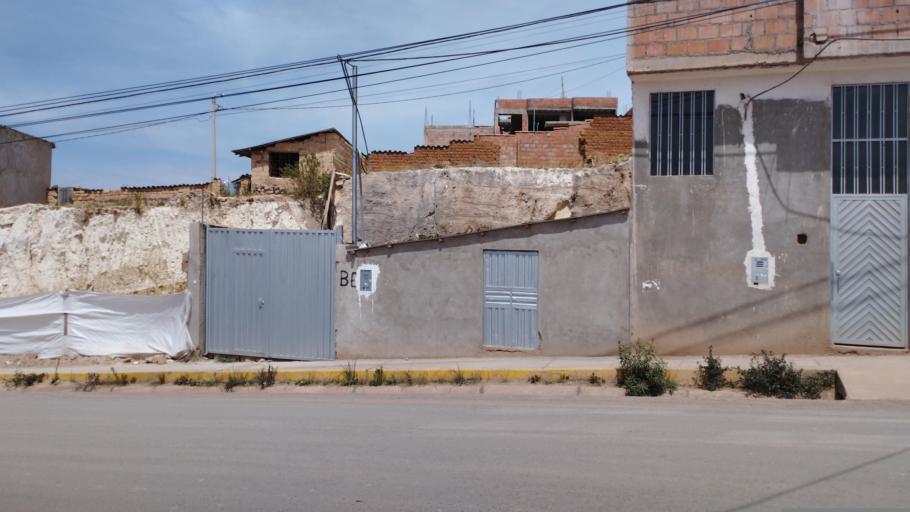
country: PE
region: Cusco
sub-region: Provincia de Cusco
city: Cusco
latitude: -13.5229
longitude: -71.9275
